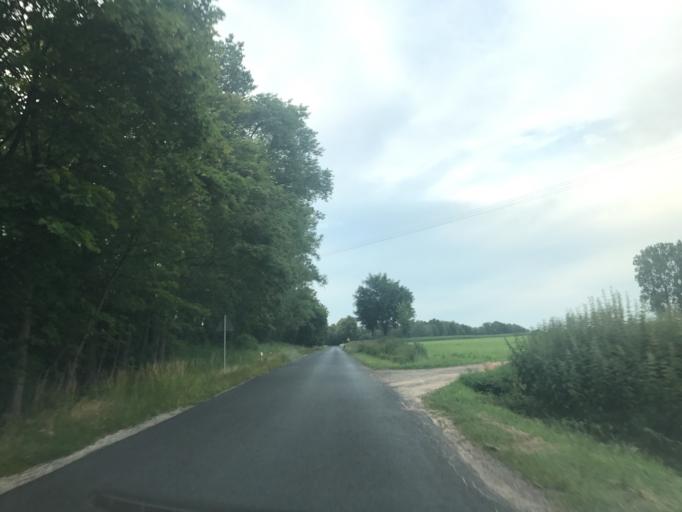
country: PL
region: Kujawsko-Pomorskie
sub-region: Powiat lipnowski
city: Lipno
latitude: 52.8137
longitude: 19.1839
